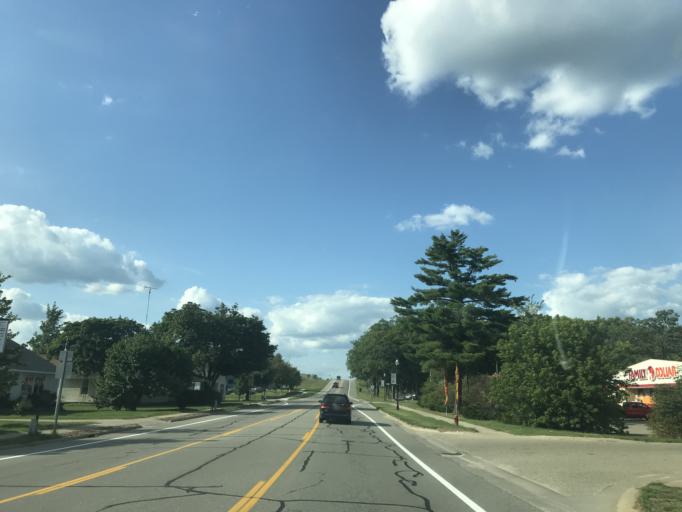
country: US
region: Michigan
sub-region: Newaygo County
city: White Cloud
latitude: 43.5527
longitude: -85.7716
